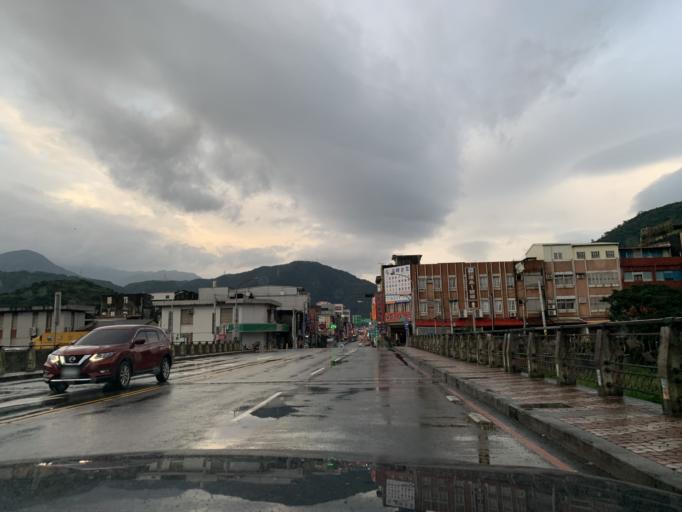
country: TW
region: Taiwan
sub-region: Yilan
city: Yilan
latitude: 24.5962
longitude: 121.8540
